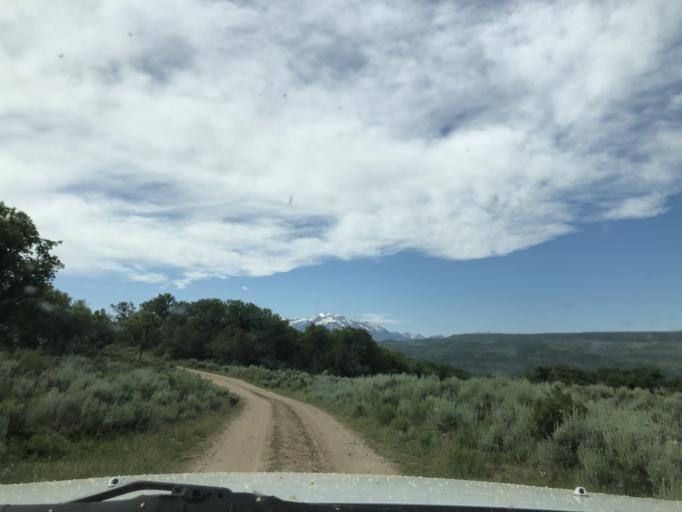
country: US
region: Colorado
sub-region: Delta County
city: Paonia
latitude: 39.0185
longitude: -107.3424
